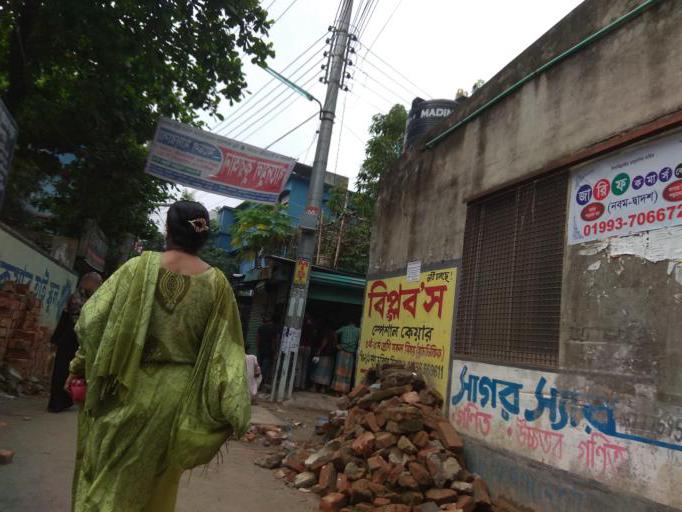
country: BD
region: Dhaka
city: Azimpur
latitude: 23.8010
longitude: 90.3665
